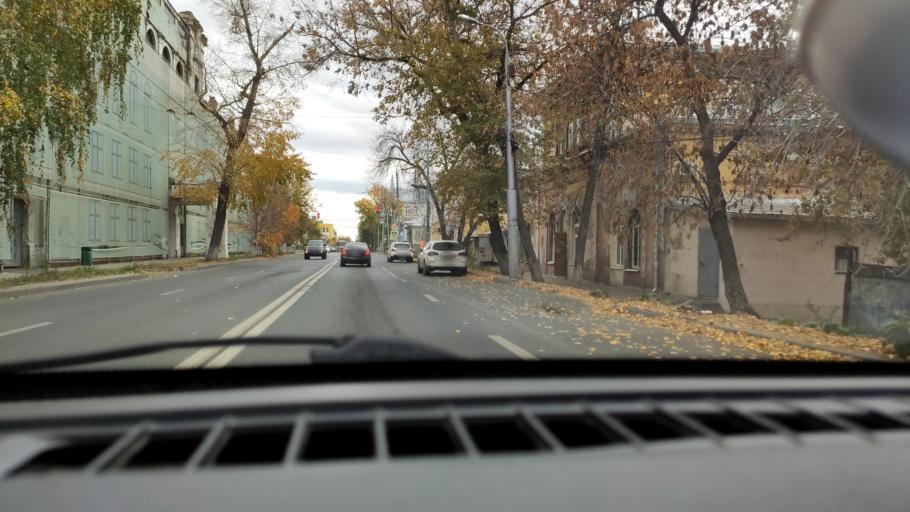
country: RU
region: Samara
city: Rozhdestveno
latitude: 53.1831
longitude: 50.0810
